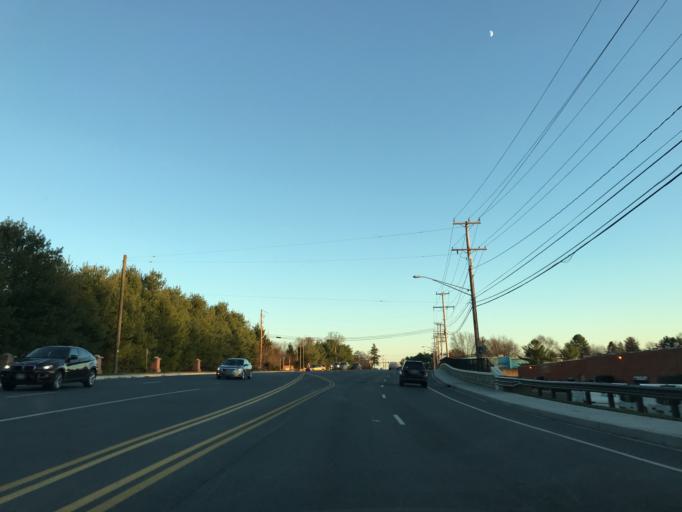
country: US
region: Maryland
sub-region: Baltimore County
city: Randallstown
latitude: 39.3786
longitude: -76.8179
